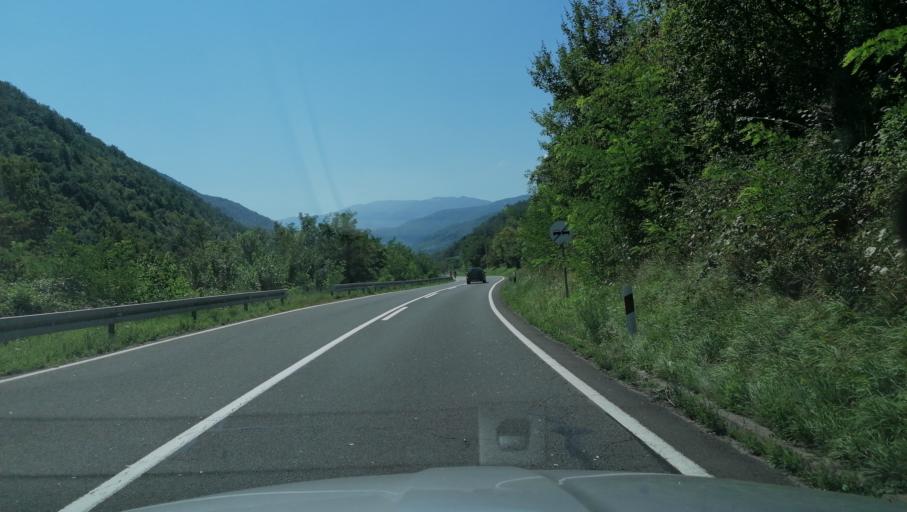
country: RS
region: Central Serbia
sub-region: Raski Okrug
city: Kraljevo
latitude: 43.6647
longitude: 20.5669
